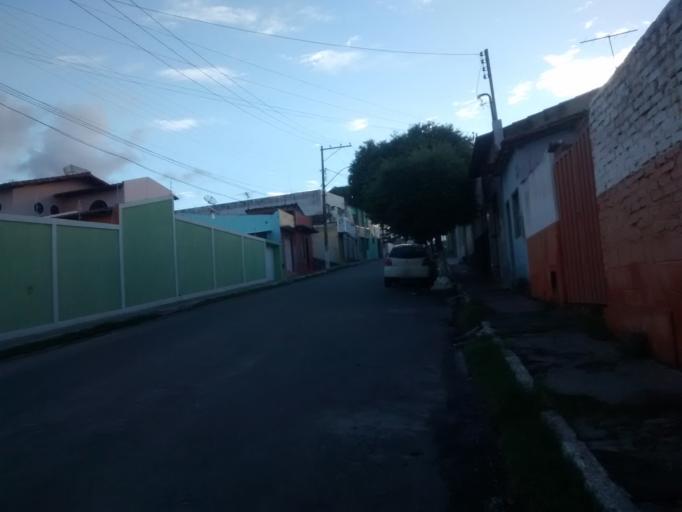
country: BR
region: Bahia
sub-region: Brumado
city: Brumado
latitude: -14.2031
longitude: -41.6650
